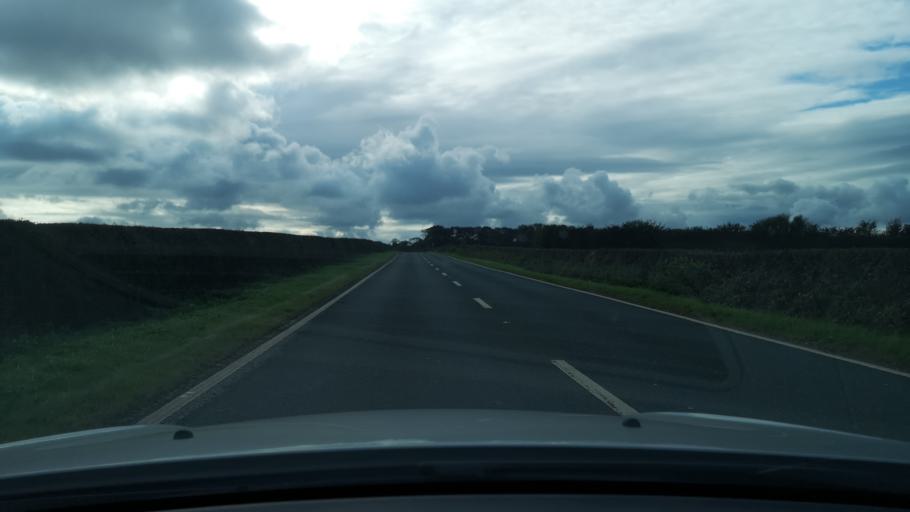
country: GB
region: England
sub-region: East Riding of Yorkshire
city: Walkington
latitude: 53.8106
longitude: -0.5343
